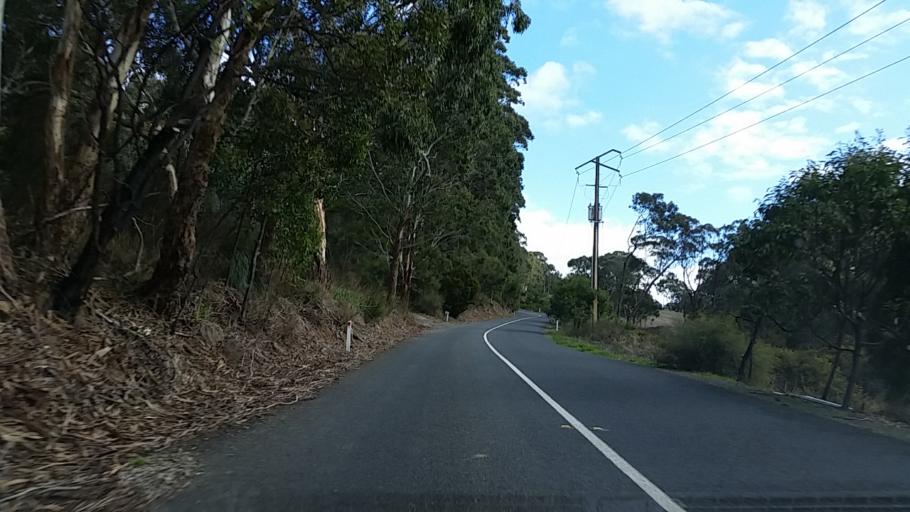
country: AU
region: South Australia
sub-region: Mount Barker
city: Little Hampton
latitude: -35.0791
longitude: 138.8279
